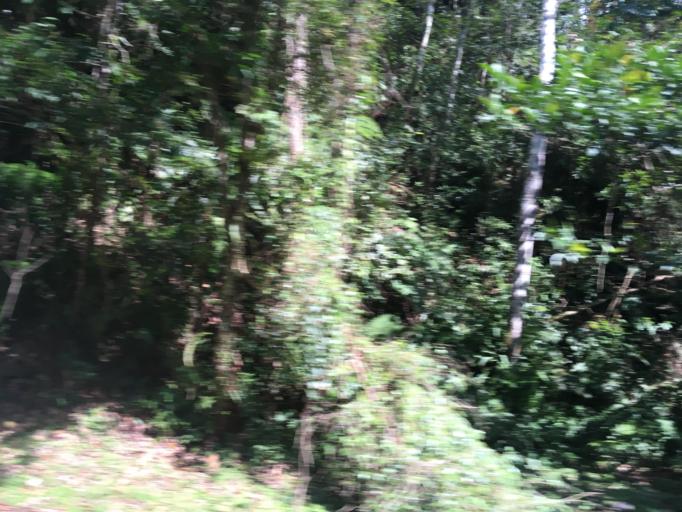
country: TW
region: Taiwan
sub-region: Yilan
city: Yilan
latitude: 24.7578
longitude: 121.6183
